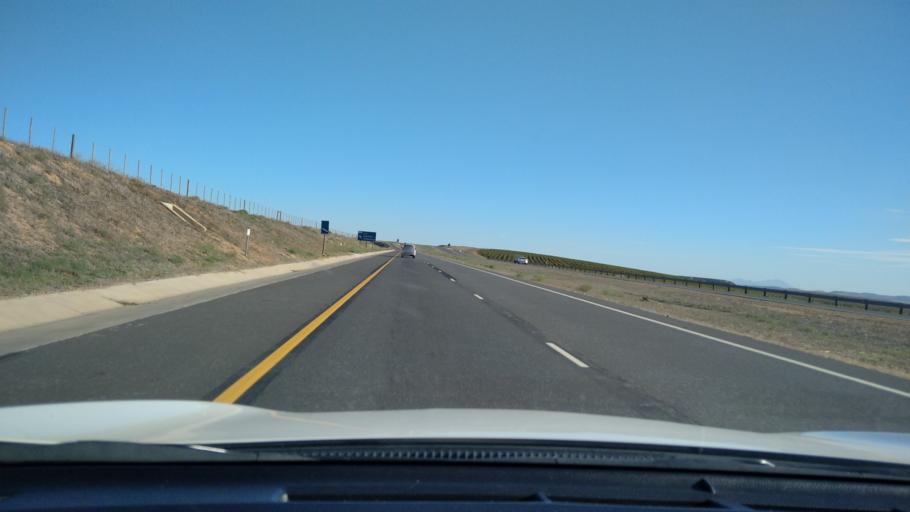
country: ZA
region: Western Cape
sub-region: West Coast District Municipality
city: Malmesbury
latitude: -33.4226
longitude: 18.7166
